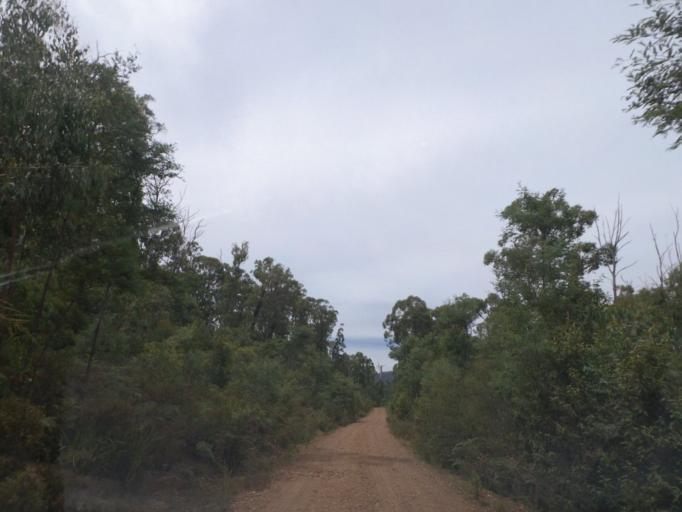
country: AU
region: Victoria
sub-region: Yarra Ranges
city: Healesville
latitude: -37.4362
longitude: 145.5805
